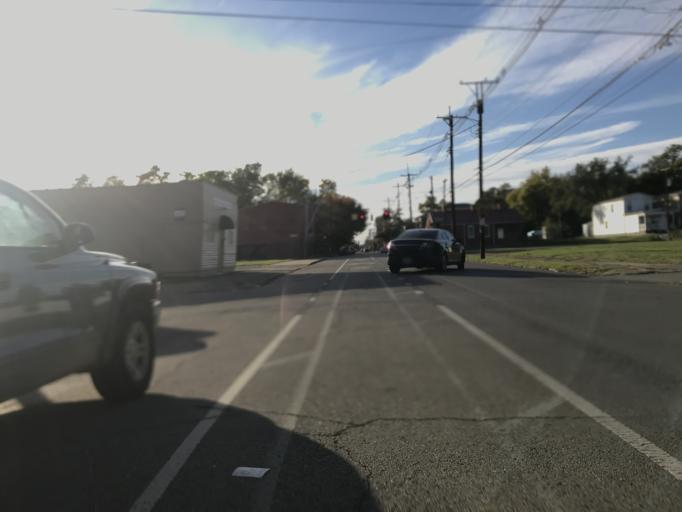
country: US
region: Kentucky
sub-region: Jefferson County
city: Louisville
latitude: 38.2402
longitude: -85.7436
